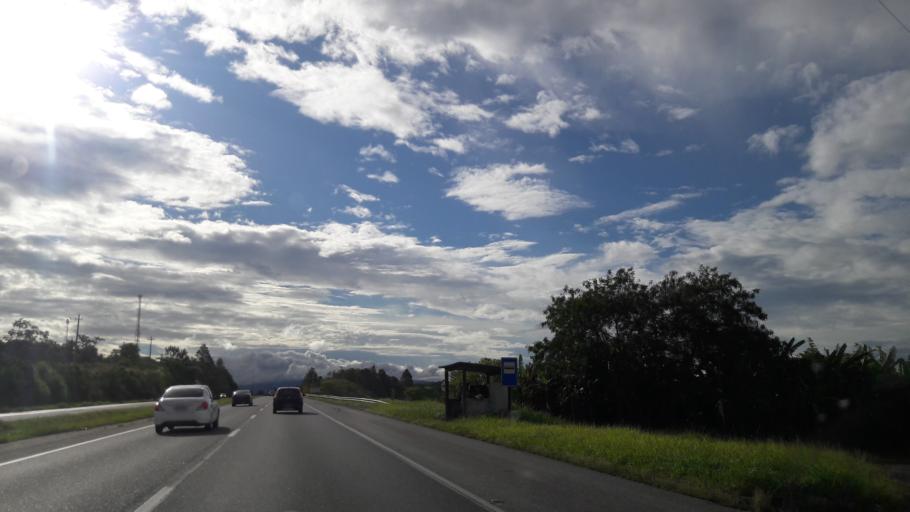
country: BR
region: Sao Paulo
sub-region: Cajati
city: Cajati
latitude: -24.7218
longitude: -48.0617
